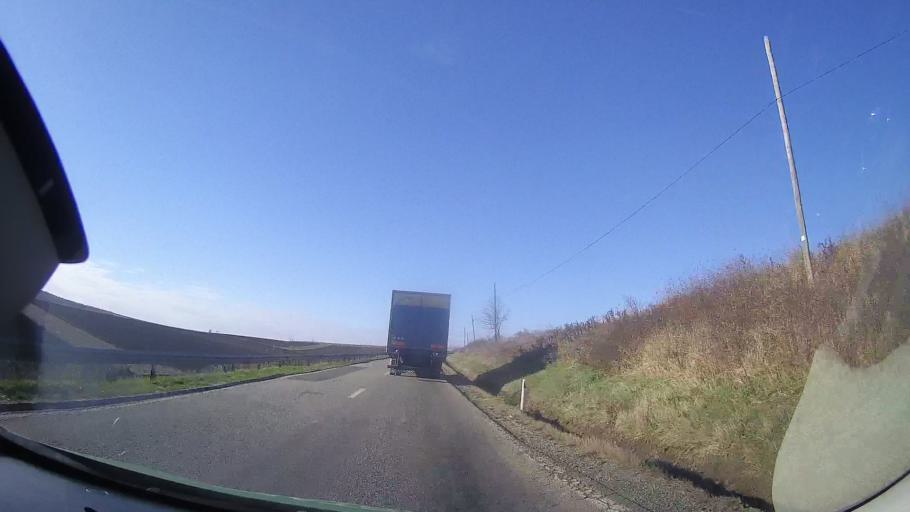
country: RO
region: Cluj
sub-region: Comuna Camarasu
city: Camarasu
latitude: 46.7934
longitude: 24.1132
